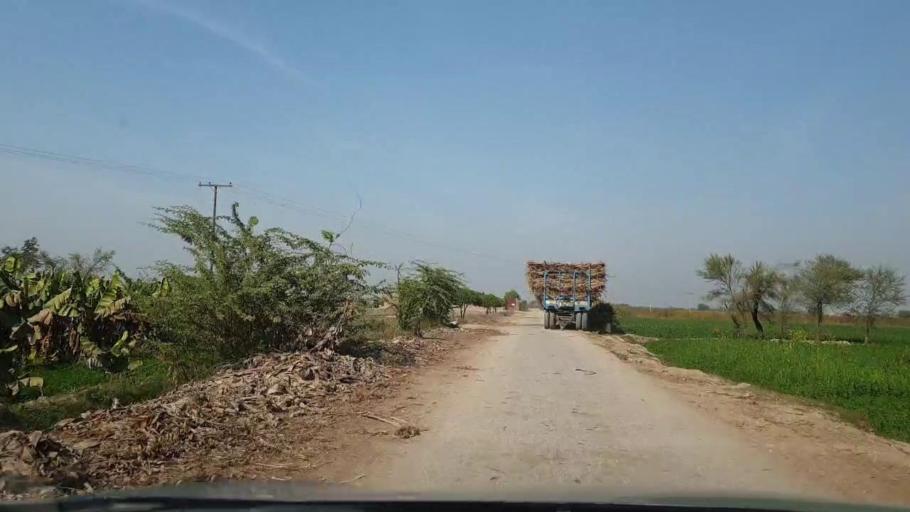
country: PK
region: Sindh
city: Berani
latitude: 25.6932
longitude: 68.7535
